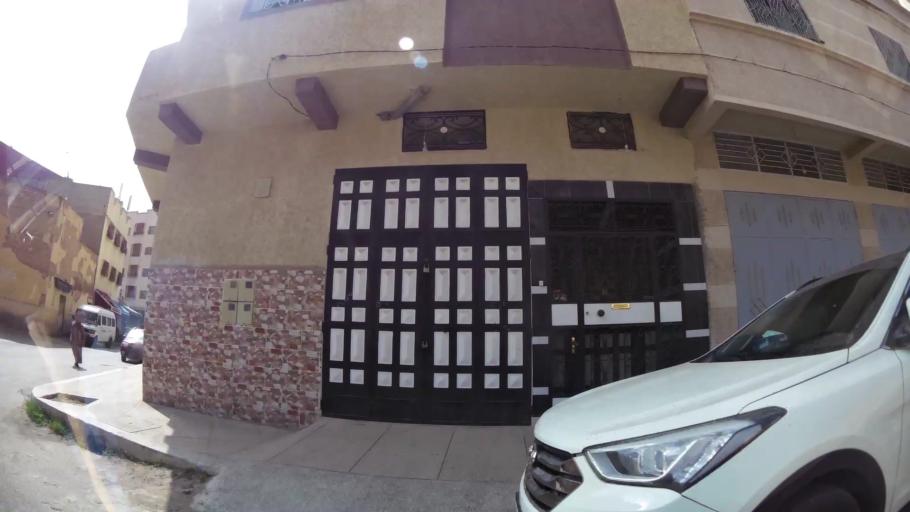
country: MA
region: Oriental
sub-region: Oujda-Angad
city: Oujda
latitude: 34.6852
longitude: -1.9107
